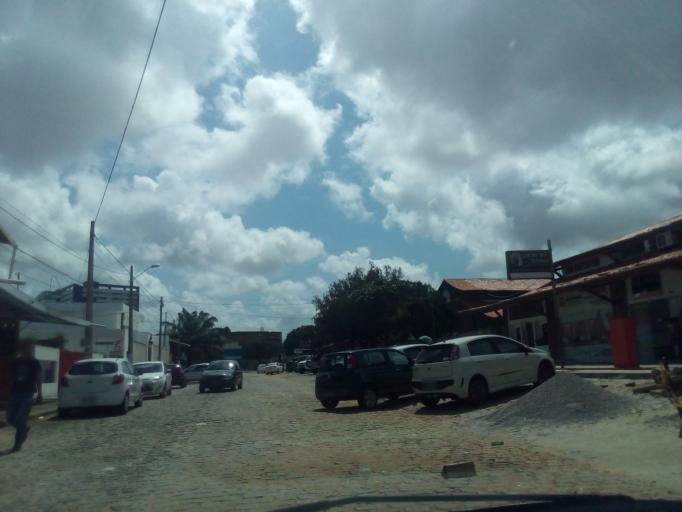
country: BR
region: Rio Grande do Norte
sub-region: Natal
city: Natal
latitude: -5.8510
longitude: -35.2031
